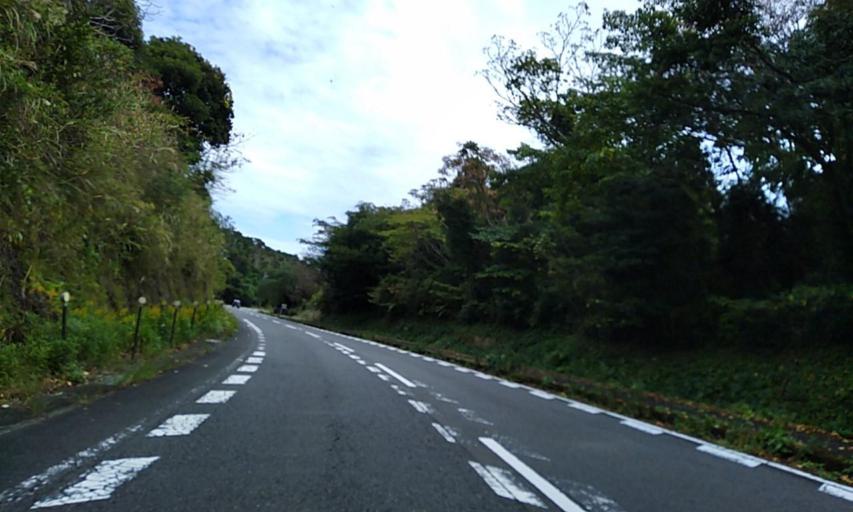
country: JP
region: Wakayama
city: Shingu
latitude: 33.4709
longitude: 135.8090
